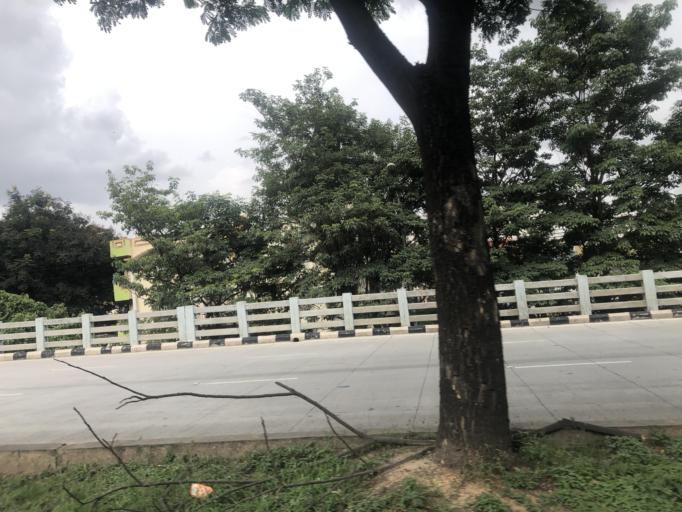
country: IN
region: Karnataka
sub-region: Bangalore Urban
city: Bangalore
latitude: 12.9658
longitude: 77.5124
